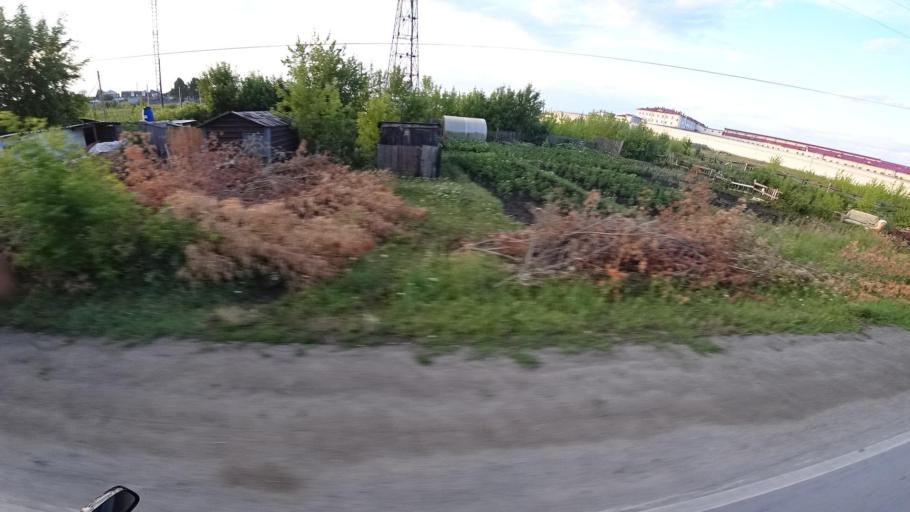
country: RU
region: Sverdlovsk
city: Kamyshlov
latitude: 56.8567
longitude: 62.7325
